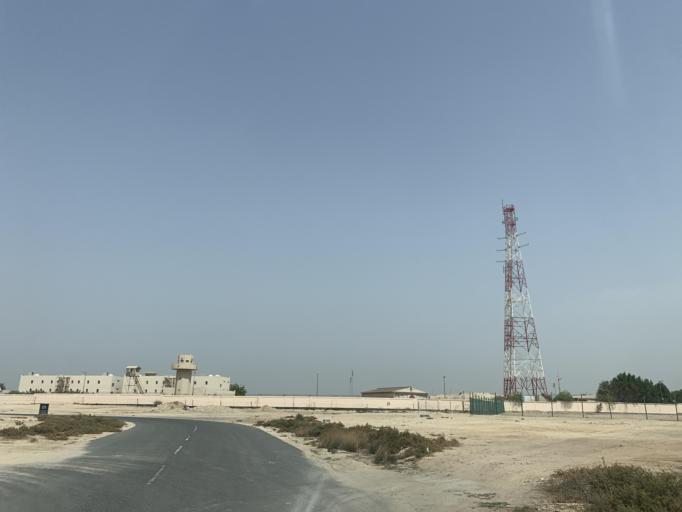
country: BH
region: Central Governorate
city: Madinat Hamad
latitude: 26.1583
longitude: 50.4801
